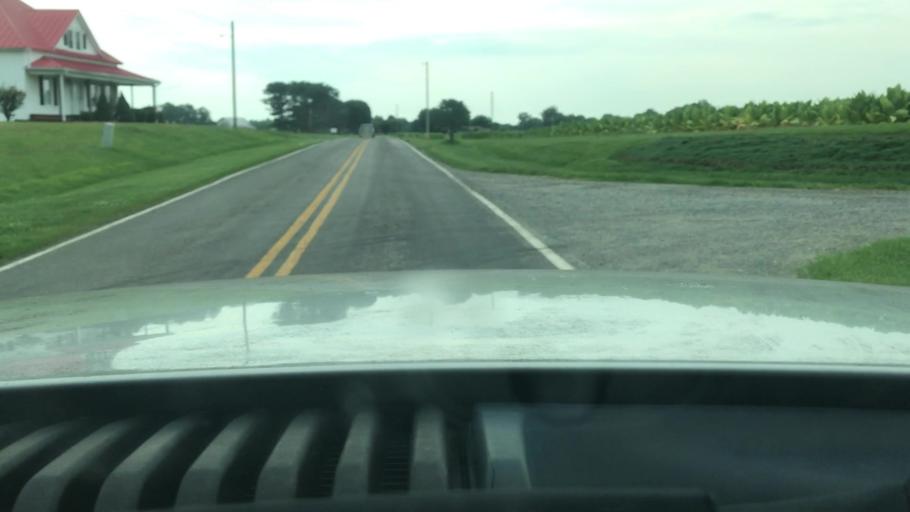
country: US
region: North Carolina
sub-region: Surry County
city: Dobson
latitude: 36.4006
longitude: -80.8029
